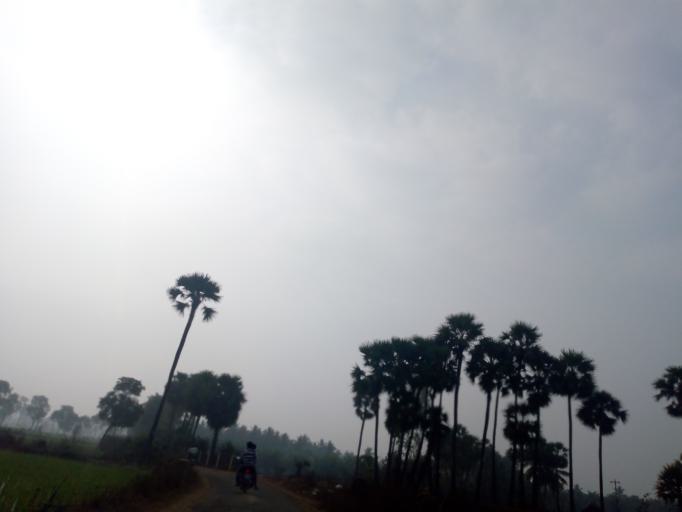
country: IN
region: Andhra Pradesh
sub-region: West Godavari
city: Tadepallegudem
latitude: 16.8434
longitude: 81.3404
